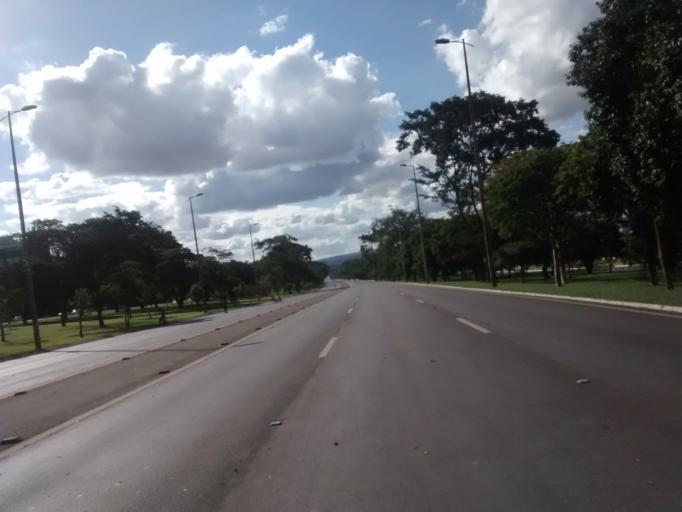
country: BR
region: Federal District
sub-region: Brasilia
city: Brasilia
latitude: -15.7688
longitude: -47.8821
